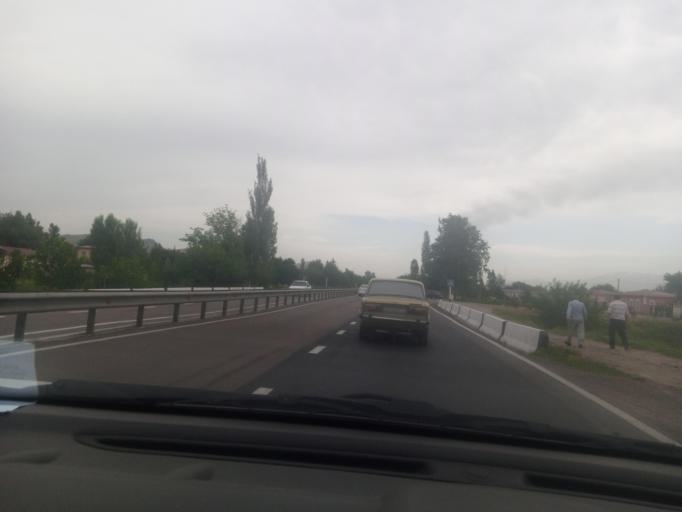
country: UZ
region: Toshkent
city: Ohangaron
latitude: 40.9067
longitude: 69.7378
